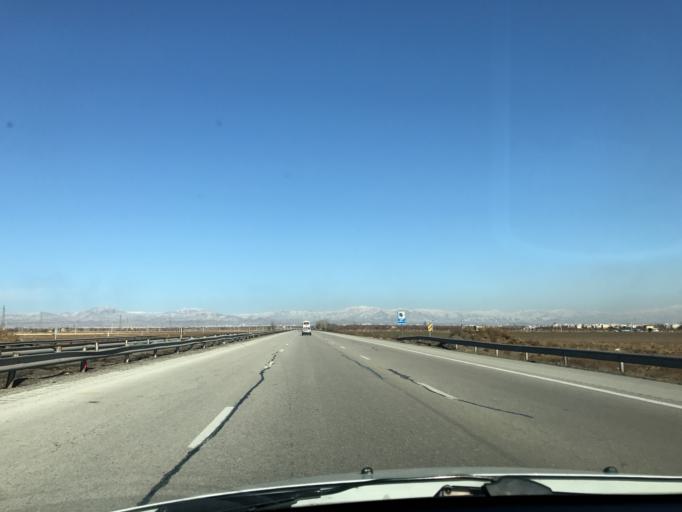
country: IR
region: Qazvin
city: Qazvin
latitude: 36.2274
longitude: 49.8936
